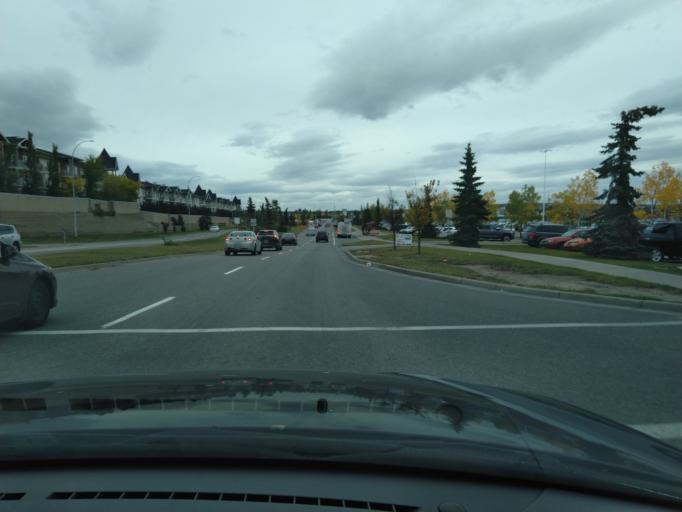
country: CA
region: Alberta
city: Calgary
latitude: 51.1567
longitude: -114.0696
